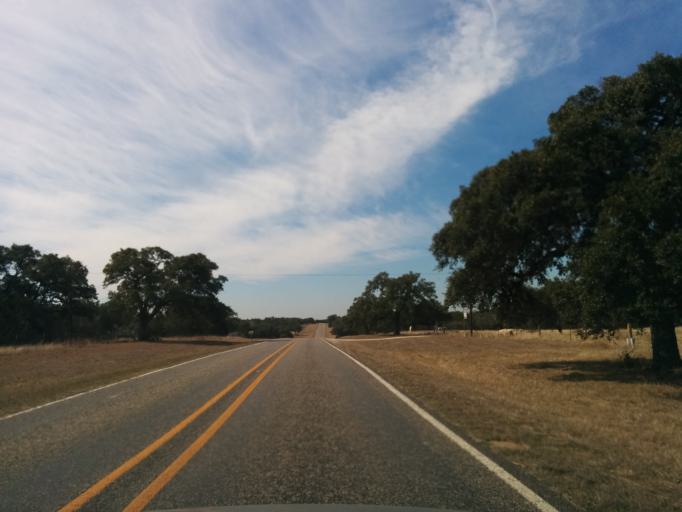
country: US
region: Texas
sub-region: Blanco County
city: Blanco
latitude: 29.9572
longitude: -98.5432
